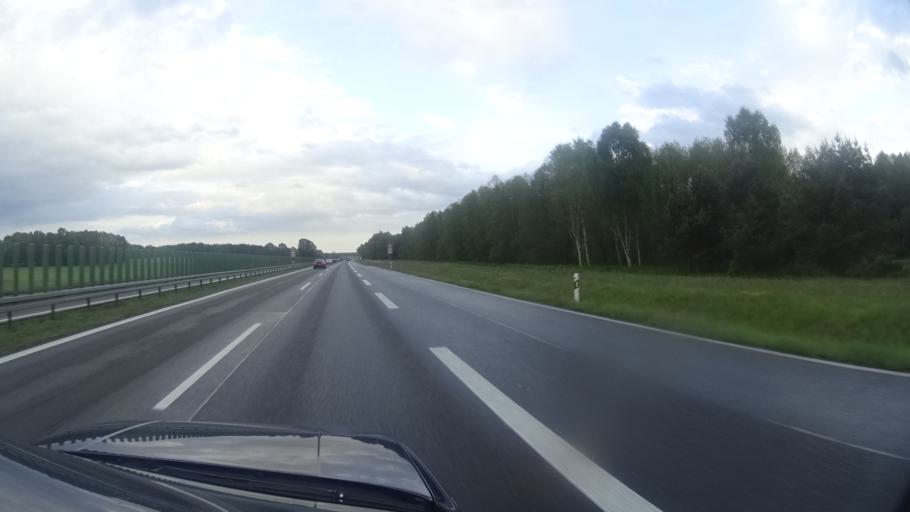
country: DE
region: Brandenburg
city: Walsleben
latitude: 52.9902
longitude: 12.6119
